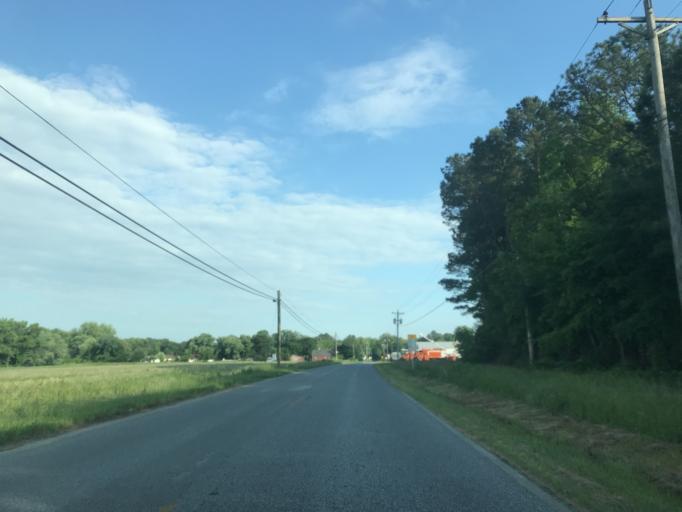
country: US
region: Maryland
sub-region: Caroline County
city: Federalsburg
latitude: 38.7169
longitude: -75.7796
